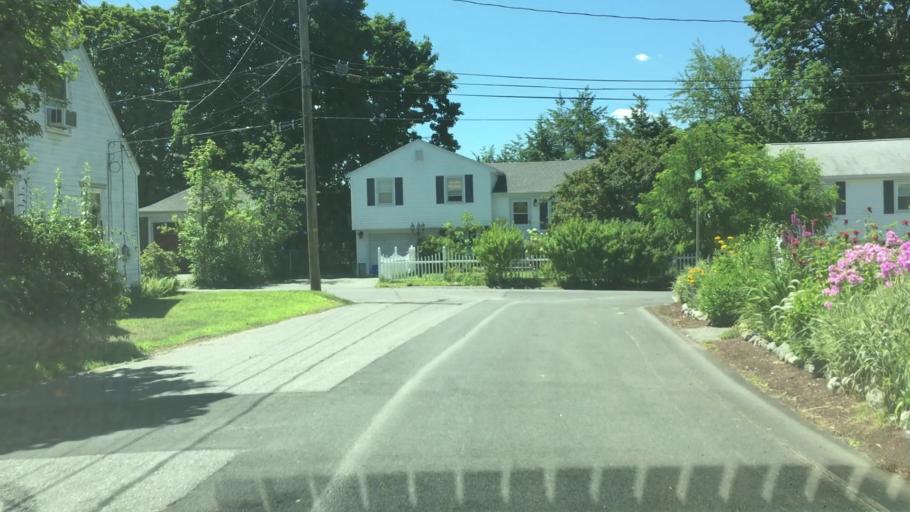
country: US
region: Massachusetts
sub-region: Middlesex County
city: Lexington
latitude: 42.4299
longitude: -71.1932
